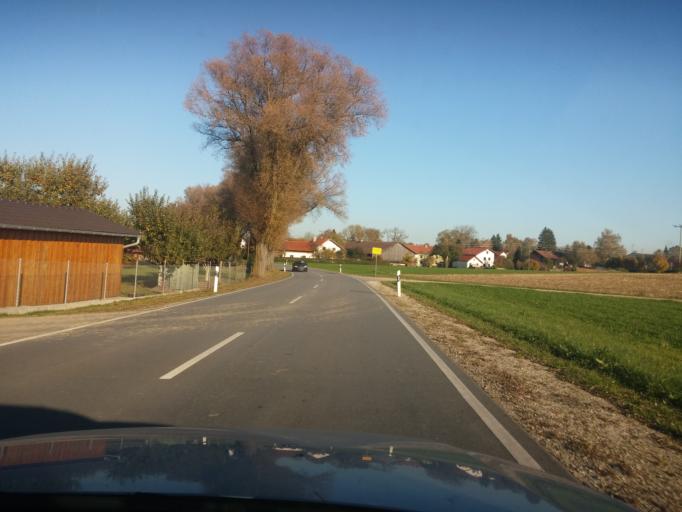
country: DE
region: Bavaria
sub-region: Upper Bavaria
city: Pastetten
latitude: 48.1980
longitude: 11.9359
